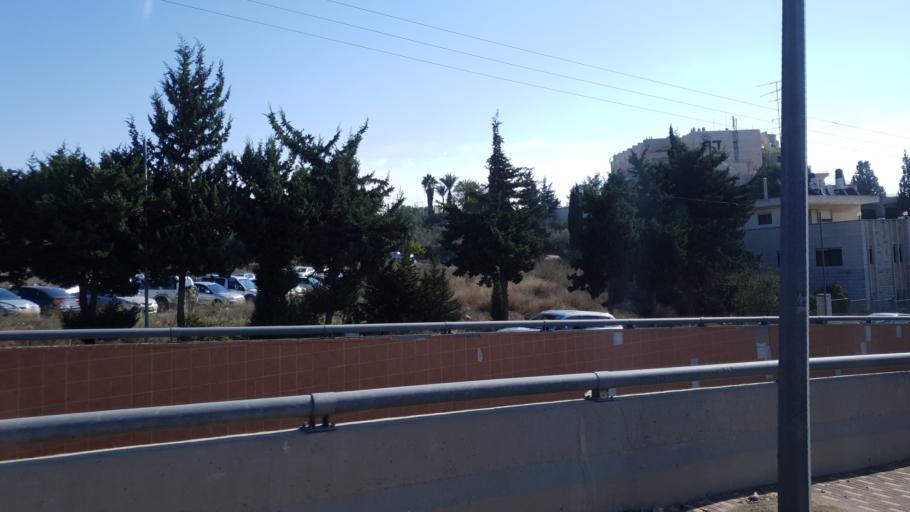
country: PS
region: West Bank
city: East Jerusalem
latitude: 31.7988
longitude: 35.2340
